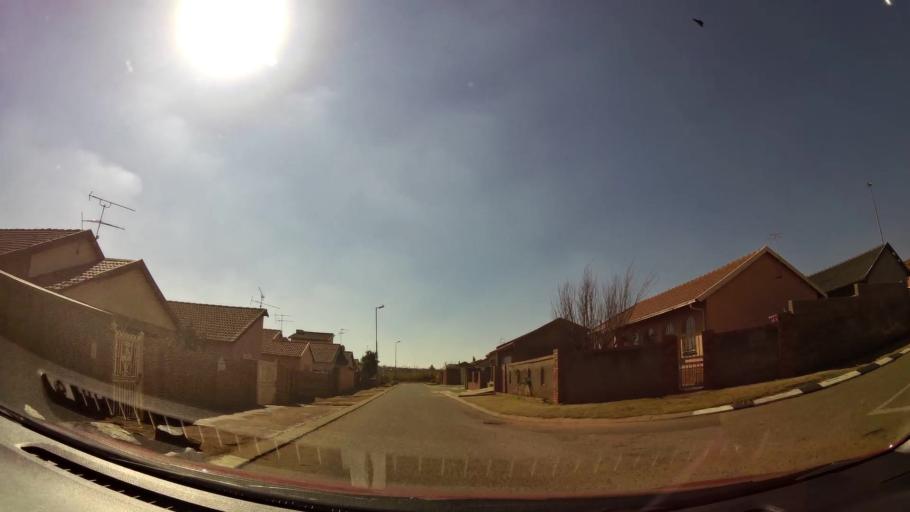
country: ZA
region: Gauteng
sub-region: City of Johannesburg Metropolitan Municipality
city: Soweto
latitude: -26.2348
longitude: 27.8198
